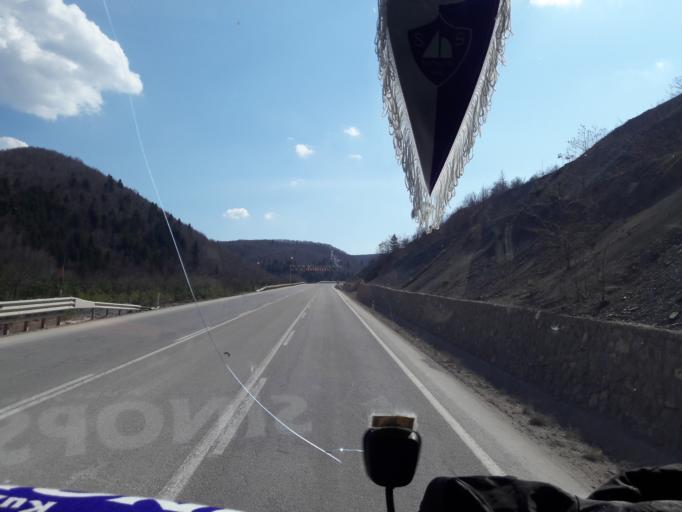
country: TR
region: Sinop
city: Boyabat
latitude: 41.6508
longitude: 34.9016
